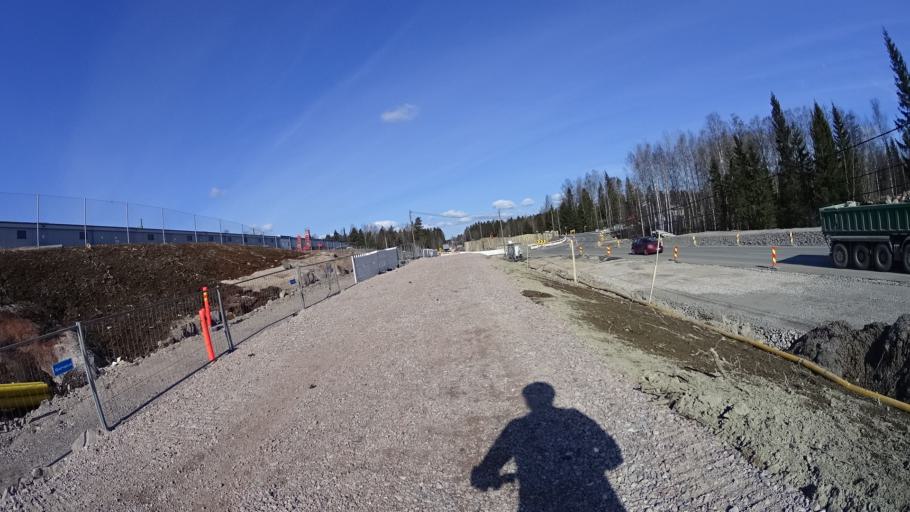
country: FI
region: Uusimaa
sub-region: Helsinki
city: Kilo
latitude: 60.2999
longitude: 24.7670
